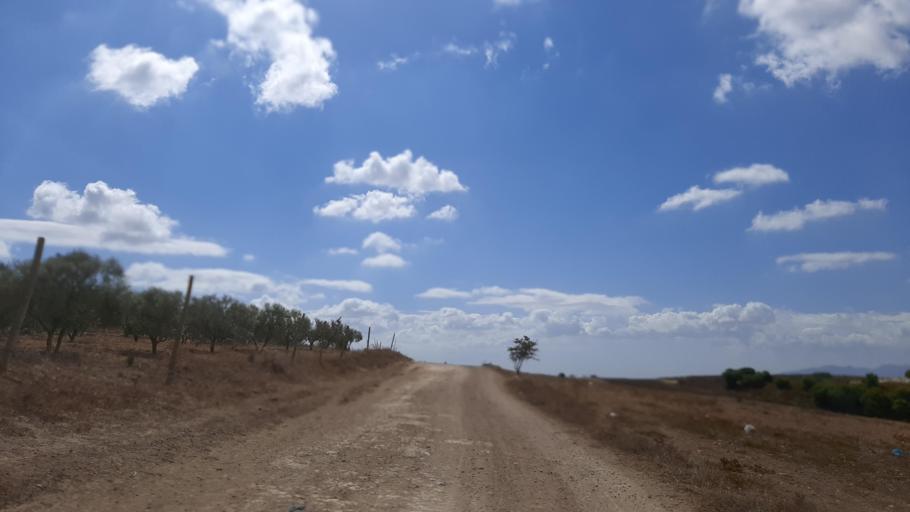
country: TN
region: Zaghwan
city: Zaghouan
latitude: 36.4861
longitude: 10.1803
